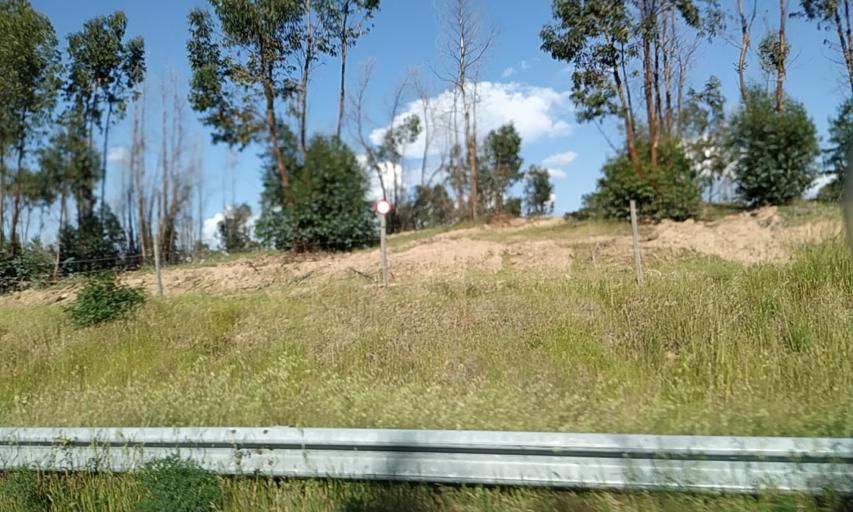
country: PT
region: Portalegre
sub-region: Fronteira
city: Fronteira
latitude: 39.0046
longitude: -7.4677
